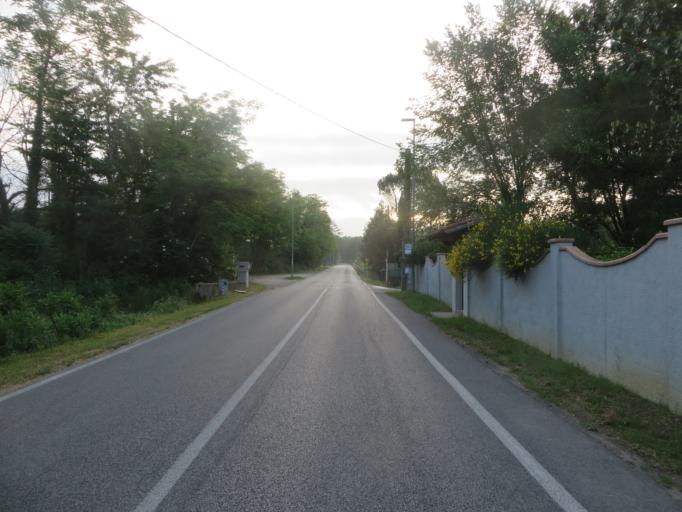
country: IT
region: Tuscany
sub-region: Province of Florence
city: Bagno a Ripoli
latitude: 43.7465
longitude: 11.3126
